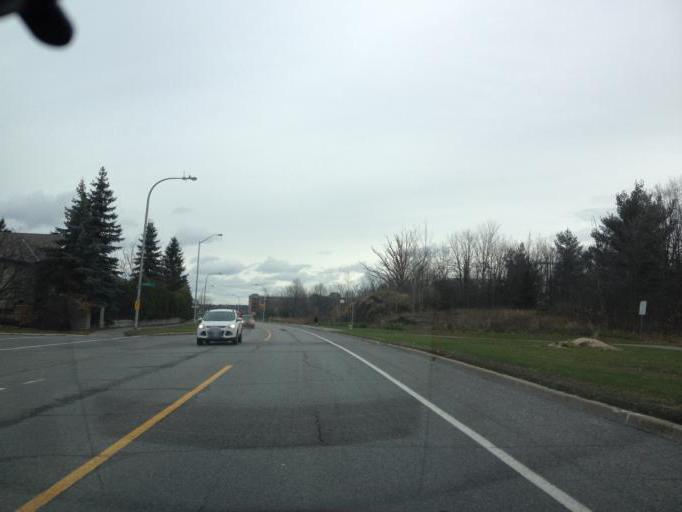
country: CA
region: Ontario
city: Bells Corners
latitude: 45.3153
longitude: -75.9071
